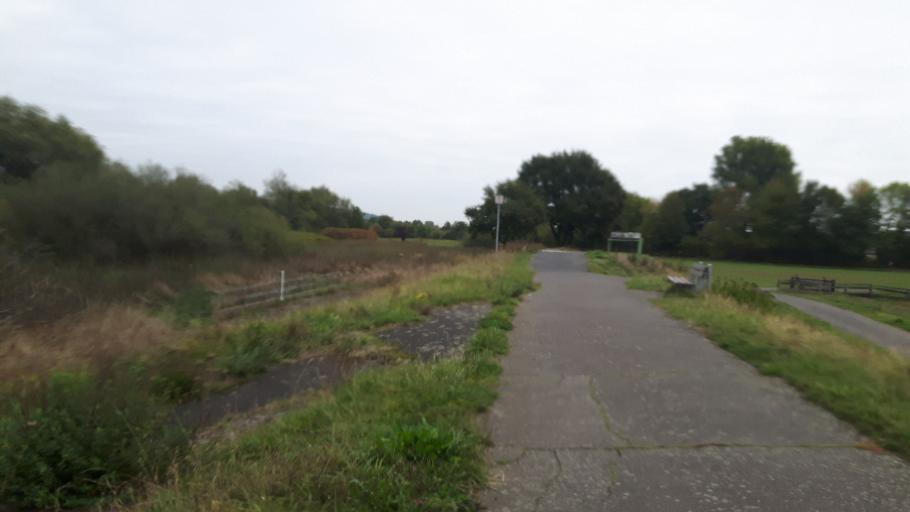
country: DE
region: North Rhine-Westphalia
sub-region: Regierungsbezirk Koln
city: Stossdorf
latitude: 50.7903
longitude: 7.2405
